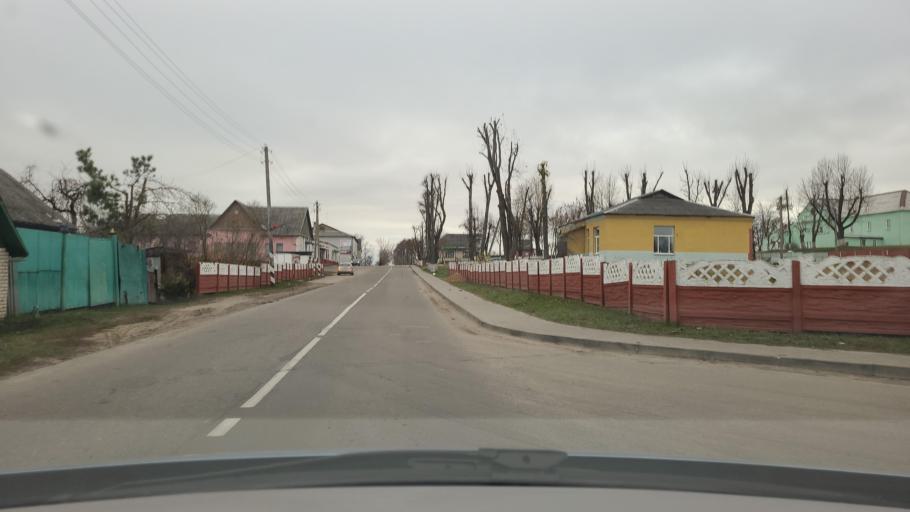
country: BY
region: Minsk
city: Khalopyenichy
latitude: 54.5189
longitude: 28.9611
